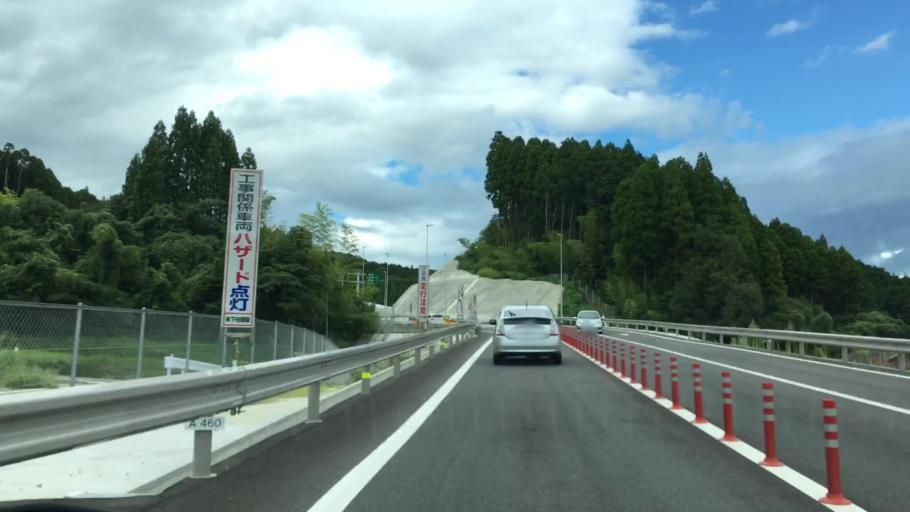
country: JP
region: Saga Prefecture
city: Imaricho-ko
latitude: 33.2950
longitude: 129.9125
